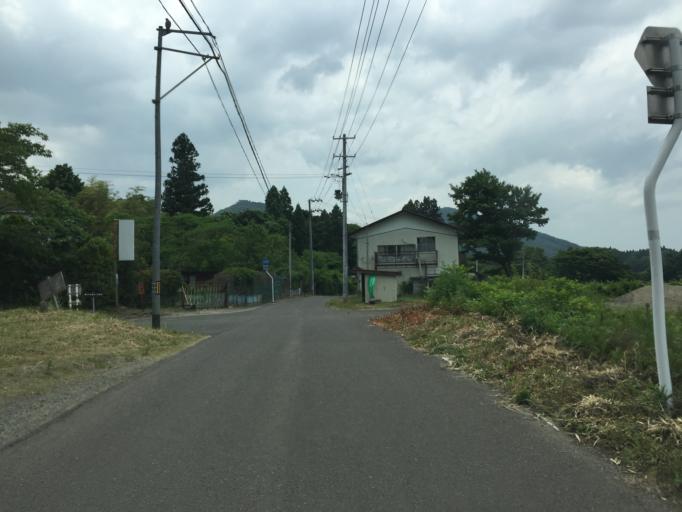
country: JP
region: Miyagi
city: Marumori
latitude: 37.8298
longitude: 140.8397
